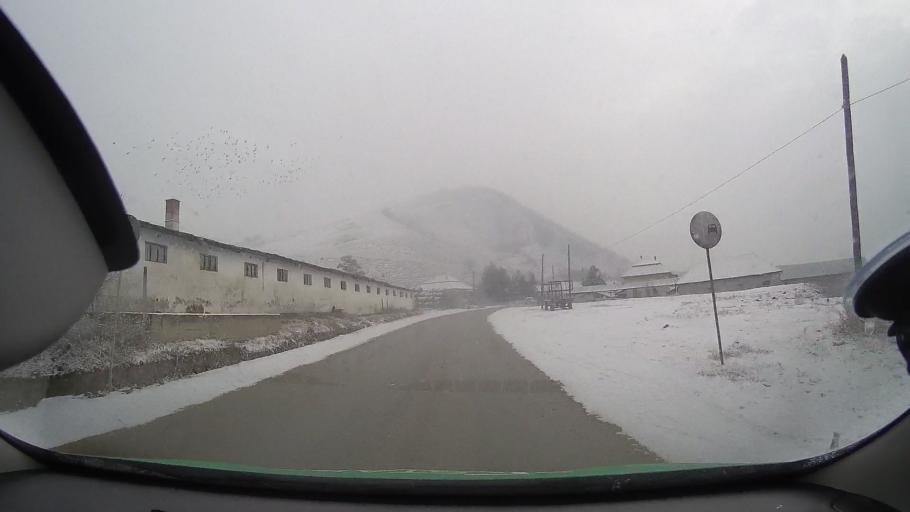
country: RO
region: Alba
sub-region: Comuna Lopadea Noua
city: Lopadea Noua
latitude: 46.2985
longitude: 23.8121
